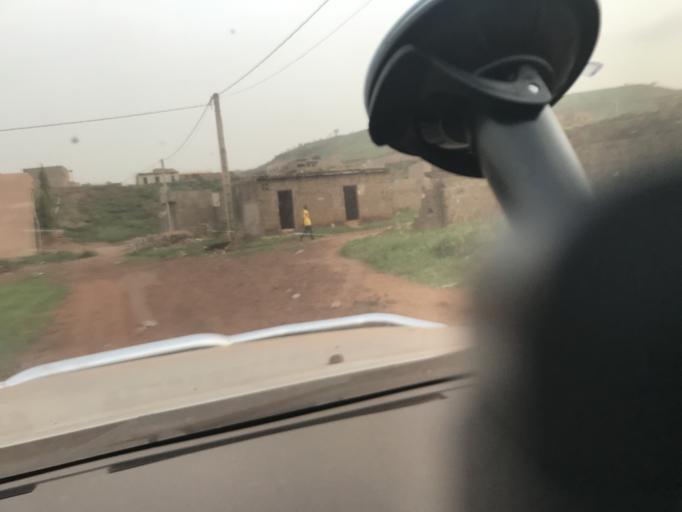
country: ML
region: Bamako
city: Bamako
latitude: 12.6492
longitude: -7.8818
